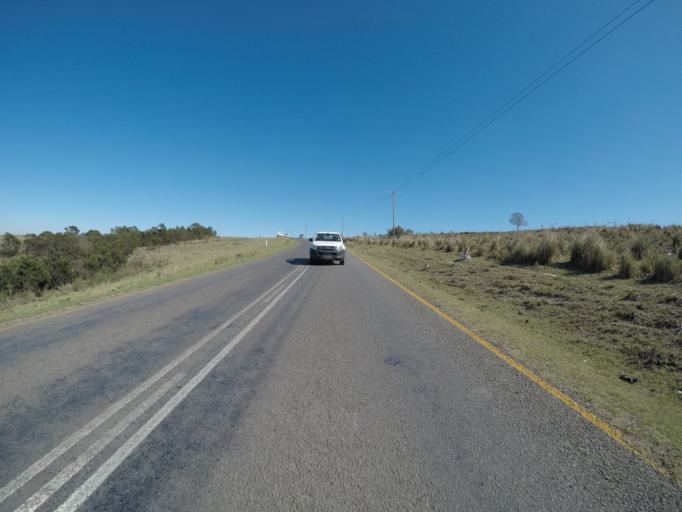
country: ZA
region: Eastern Cape
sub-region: OR Tambo District Municipality
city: Mthatha
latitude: -31.8033
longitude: 28.7526
